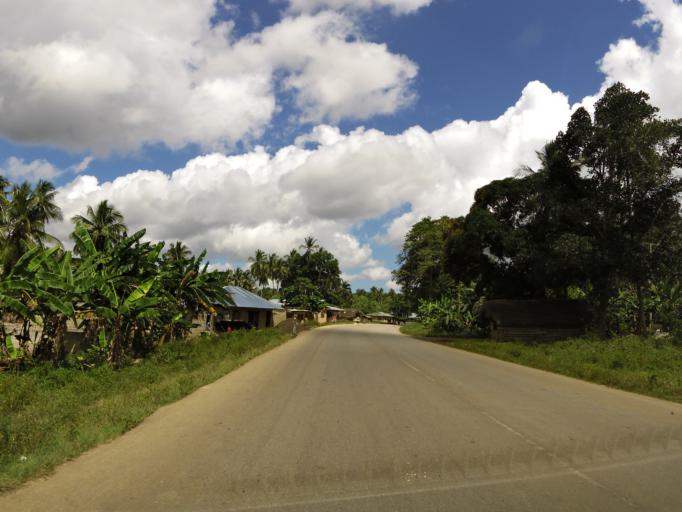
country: TZ
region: Zanzibar Central/South
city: Koani
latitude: -6.1345
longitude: 39.2946
